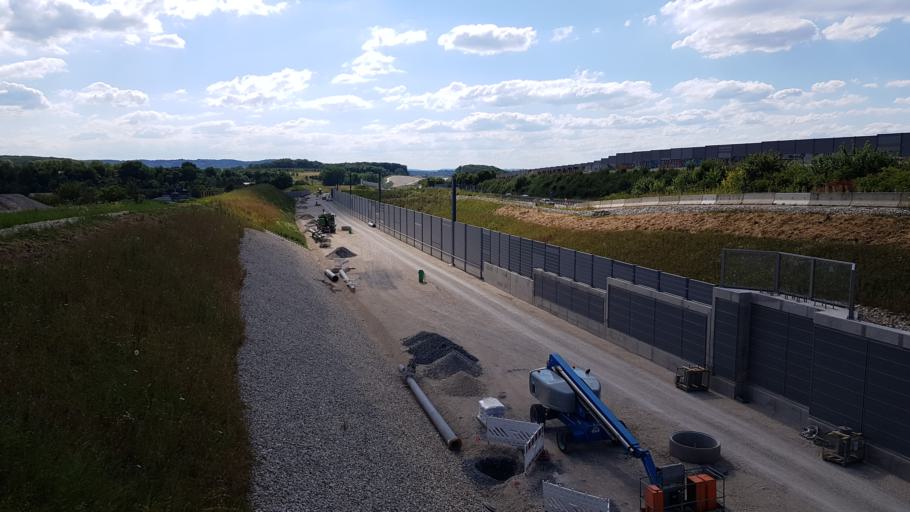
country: DE
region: Baden-Wuerttemberg
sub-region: Regierungsbezirk Stuttgart
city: Holzmaden
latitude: 48.6284
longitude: 9.5229
